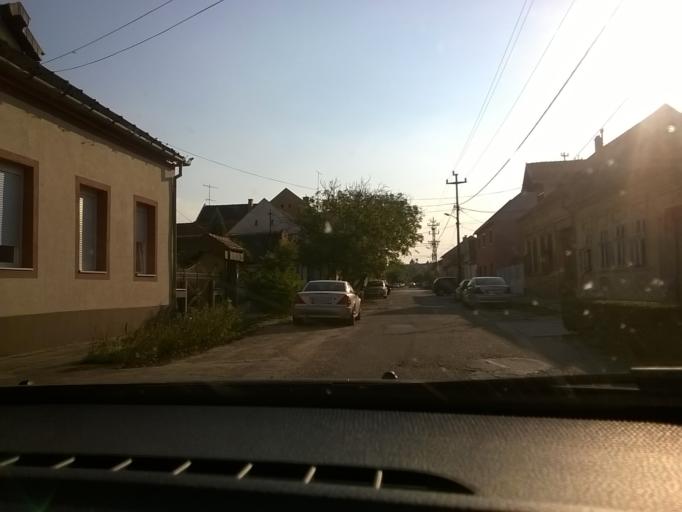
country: RS
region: Autonomna Pokrajina Vojvodina
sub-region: Juznobanatski Okrug
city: Vrsac
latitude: 45.1208
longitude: 21.2903
